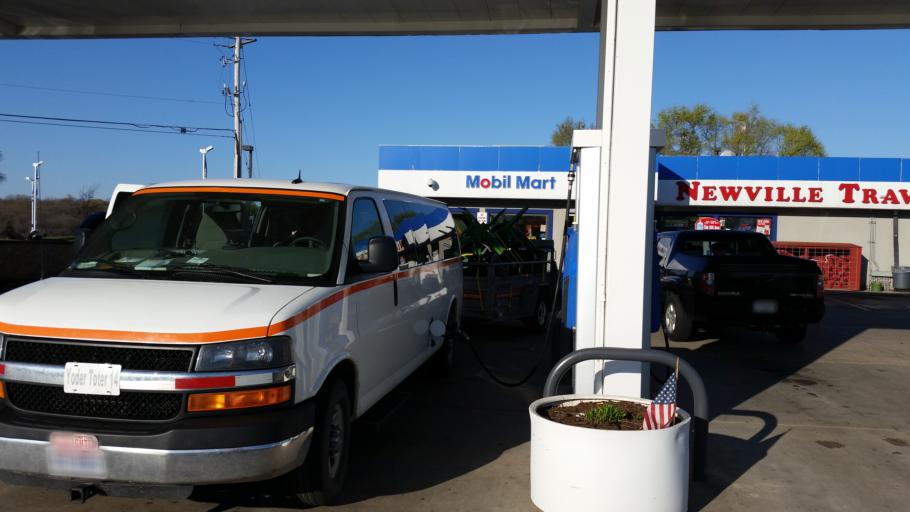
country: US
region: Wisconsin
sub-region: Rock County
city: Edgerton
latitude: 42.8333
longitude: -89.0244
